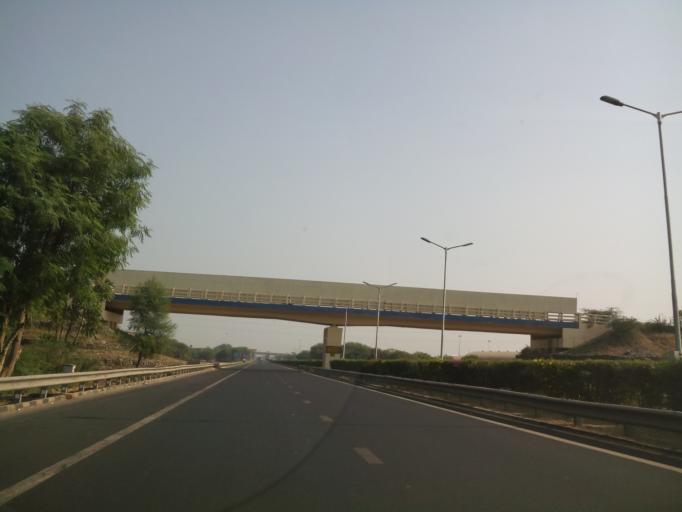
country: IN
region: Gujarat
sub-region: Ahmadabad
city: Ahmedabad
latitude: 22.9736
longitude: 72.6544
